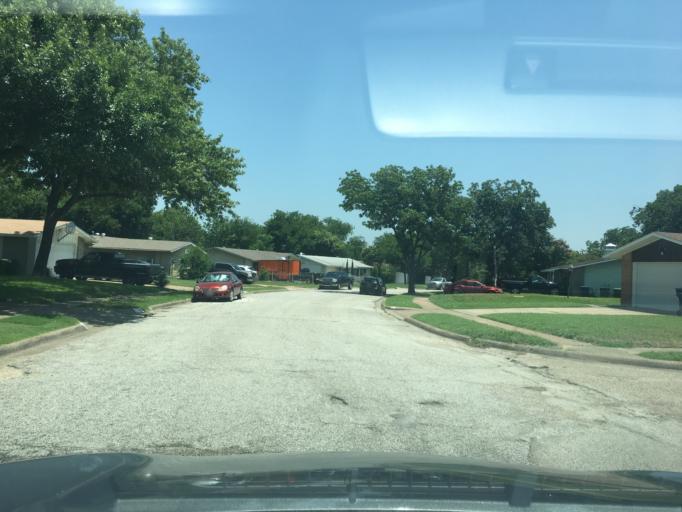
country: US
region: Texas
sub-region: Dallas County
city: Garland
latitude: 32.9121
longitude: -96.6861
